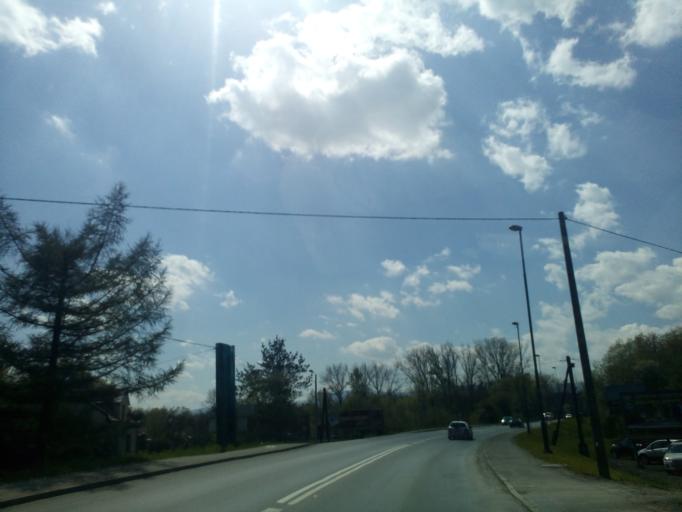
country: PL
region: Lesser Poland Voivodeship
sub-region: Powiat nowosadecki
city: Stary Sacz
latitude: 49.5707
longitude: 20.6611
